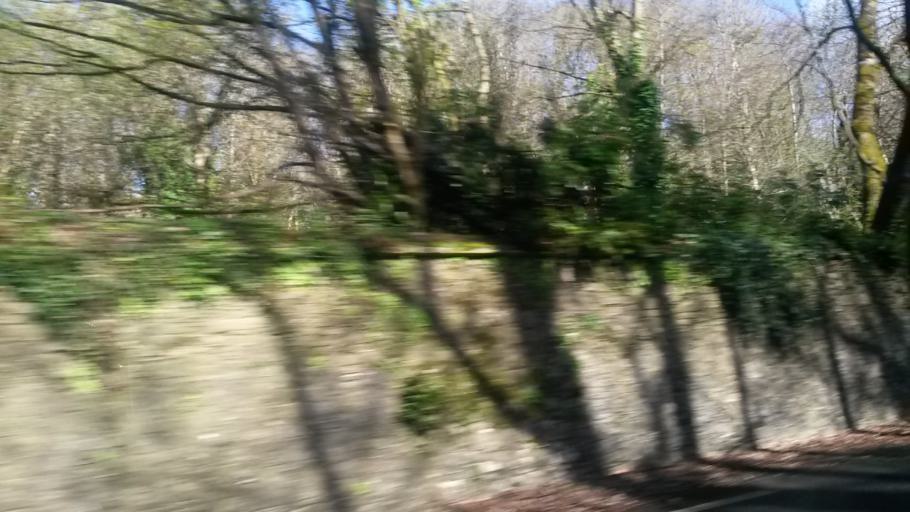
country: IE
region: Munster
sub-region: County Cork
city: Carrigtwohill
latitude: 51.8949
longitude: -8.2821
